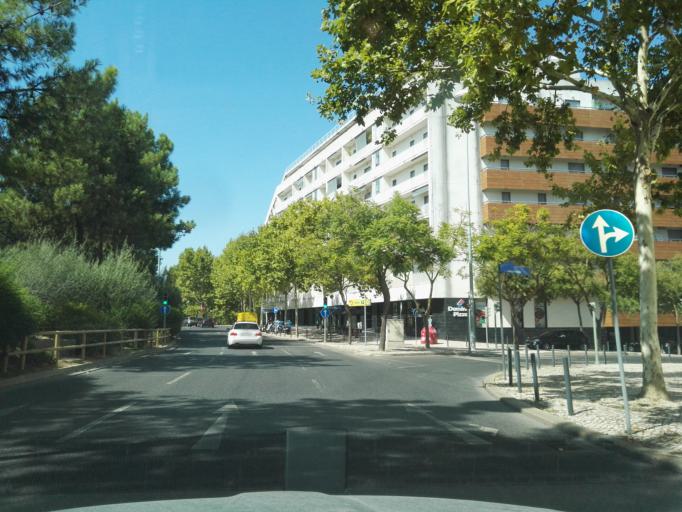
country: PT
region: Lisbon
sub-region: Loures
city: Moscavide
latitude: 38.7808
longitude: -9.0986
